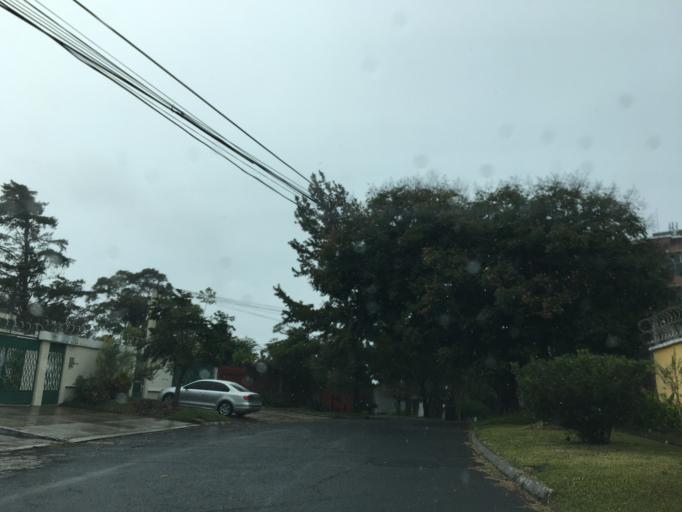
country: GT
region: Guatemala
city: Santa Catarina Pinula
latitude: 14.5841
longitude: -90.4917
